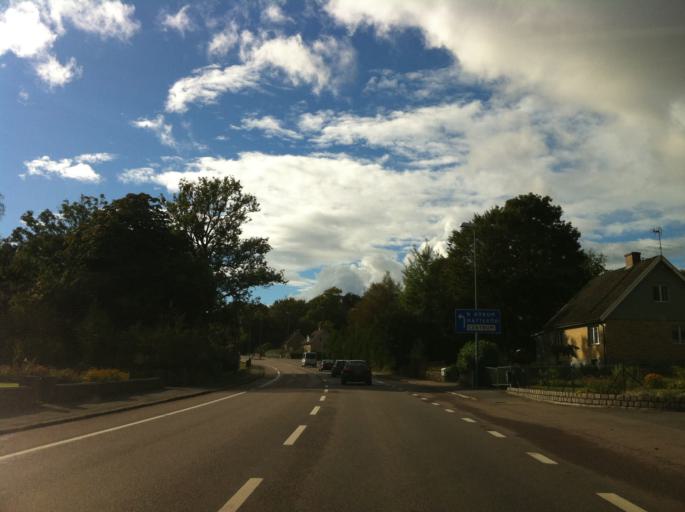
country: SE
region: Skane
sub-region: Hassleholms Kommun
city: Tormestorp
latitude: 56.1631
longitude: 13.5908
